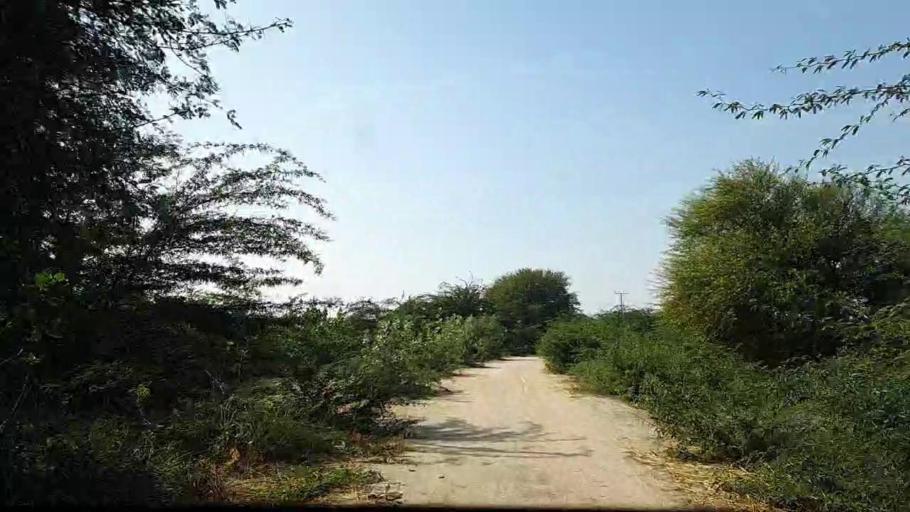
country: PK
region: Sindh
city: Daro Mehar
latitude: 24.7024
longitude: 68.1542
